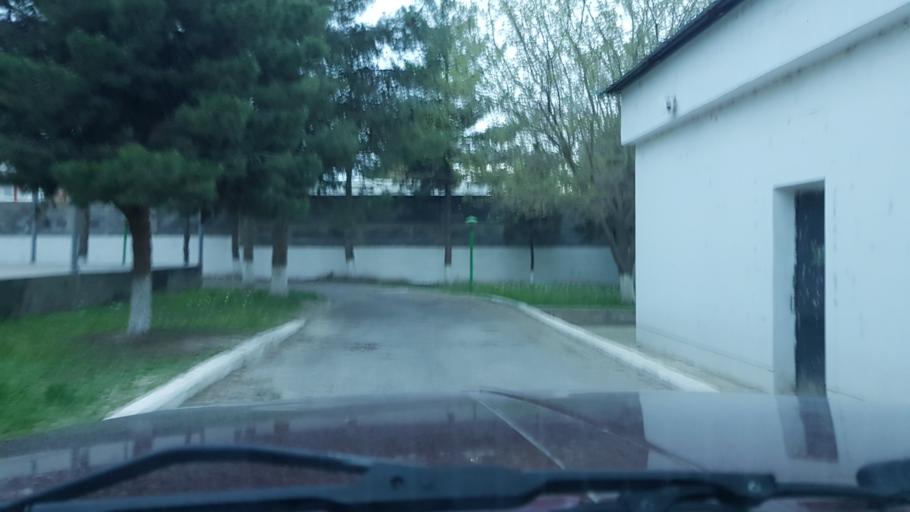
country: TM
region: Ahal
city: Ashgabat
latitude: 37.8848
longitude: 58.3629
